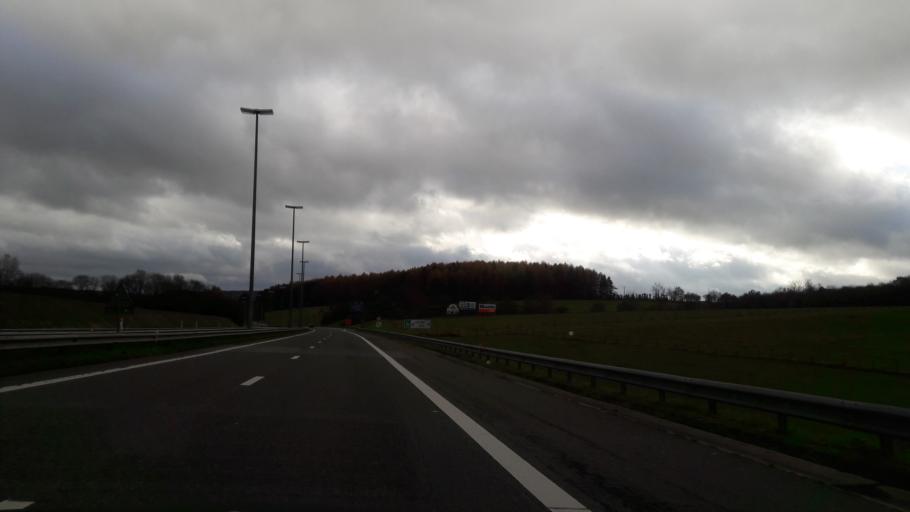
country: BE
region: Wallonia
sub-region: Province de Liege
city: Saint-Vith
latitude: 50.2736
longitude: 6.1100
